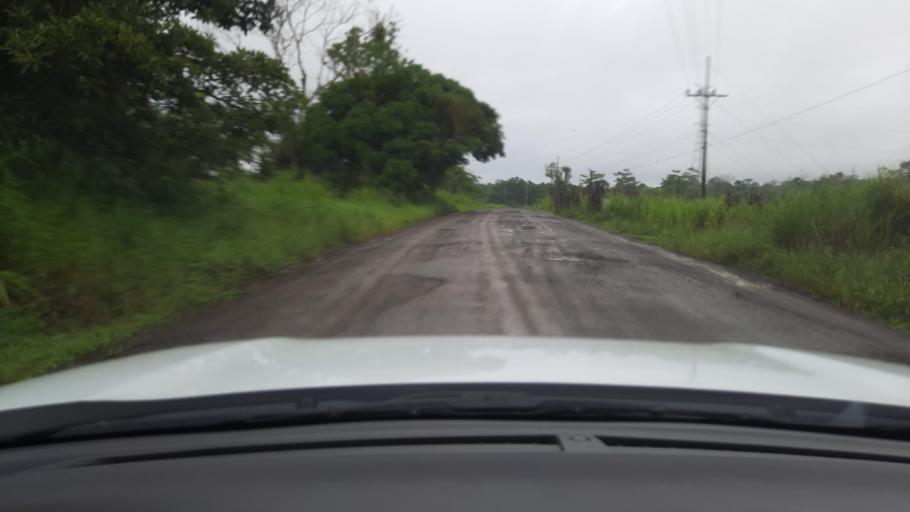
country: CR
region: Alajuela
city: San Jose
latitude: 11.0111
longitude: -85.3253
